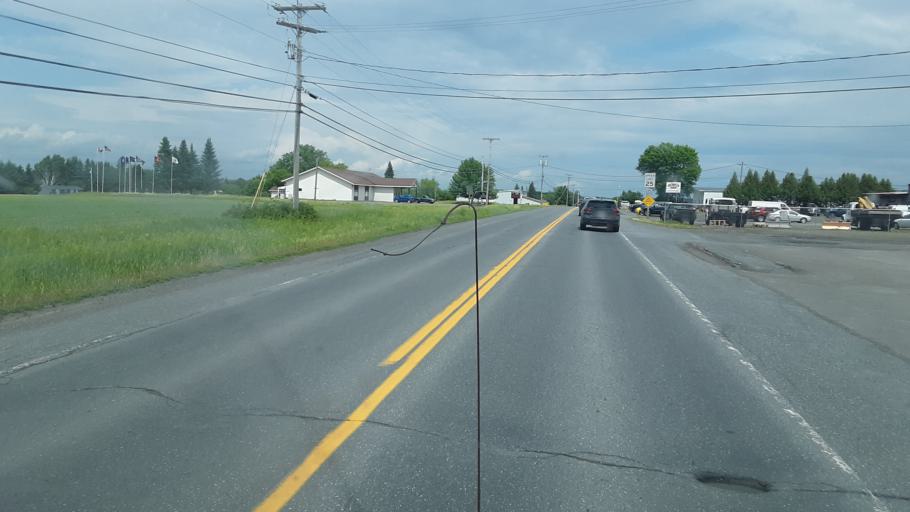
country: US
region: Maine
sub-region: Aroostook County
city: Fort Fairfield
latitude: 46.7662
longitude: -67.8475
